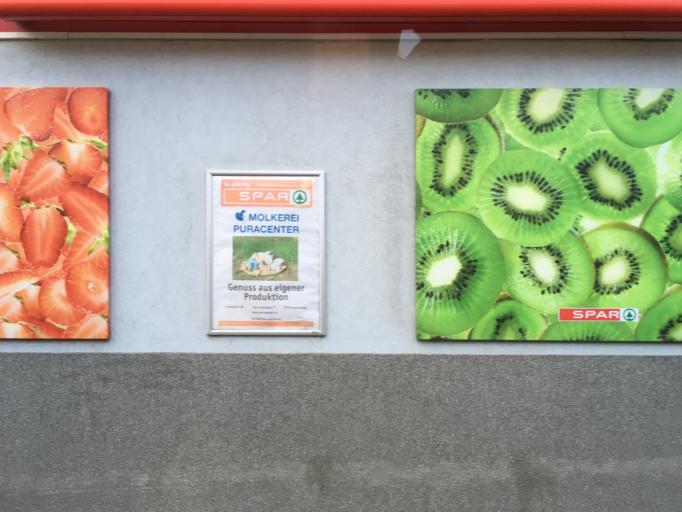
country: CH
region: Grisons
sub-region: Plessur District
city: Churwalden
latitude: 46.7250
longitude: 9.5580
